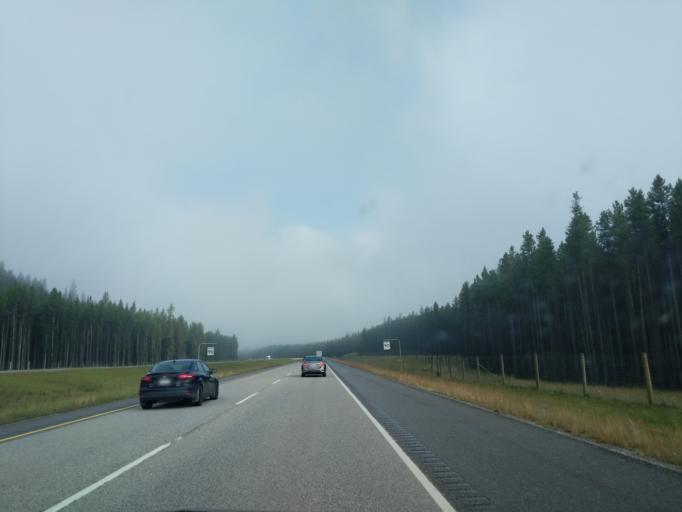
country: CA
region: Alberta
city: Lake Louise
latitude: 51.2803
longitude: -115.9707
